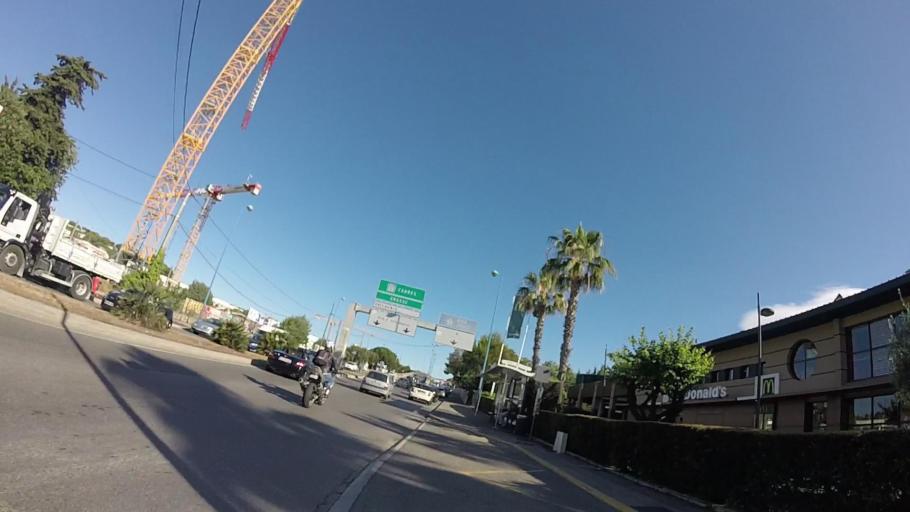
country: FR
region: Provence-Alpes-Cote d'Azur
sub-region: Departement des Alpes-Maritimes
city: Biot
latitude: 43.5996
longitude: 7.0864
